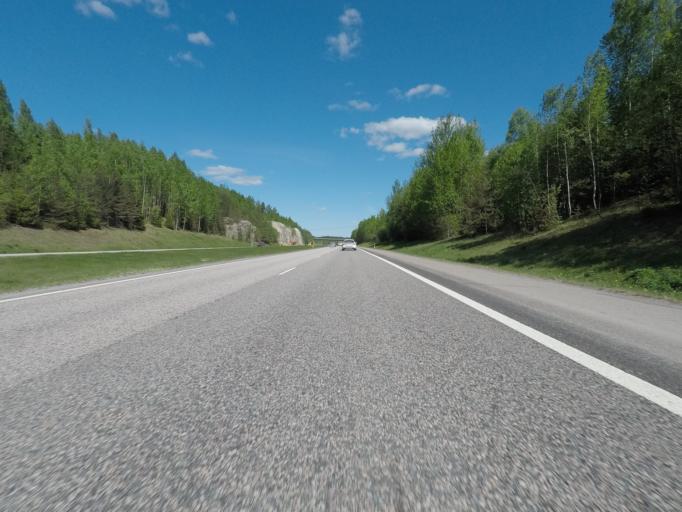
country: FI
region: Uusimaa
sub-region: Helsinki
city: Nurmijaervi
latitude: 60.3849
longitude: 24.8154
